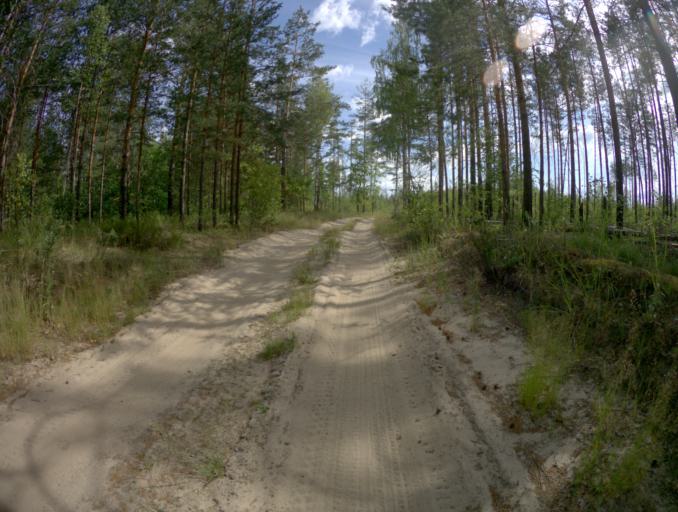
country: RU
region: Ivanovo
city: Talitsy
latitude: 56.5312
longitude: 42.4094
